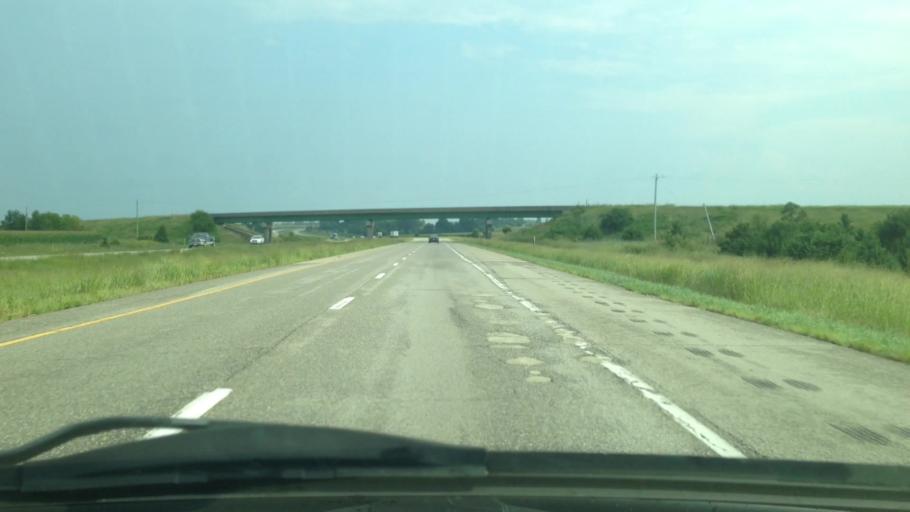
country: US
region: Iowa
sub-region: Benton County
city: Urbana
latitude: 42.2837
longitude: -91.9433
